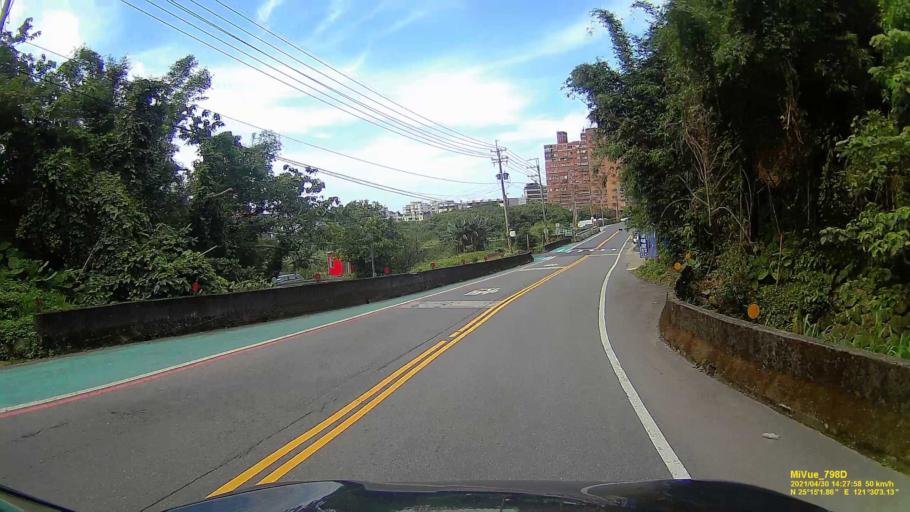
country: TW
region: Taipei
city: Taipei
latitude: 25.2509
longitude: 121.5011
